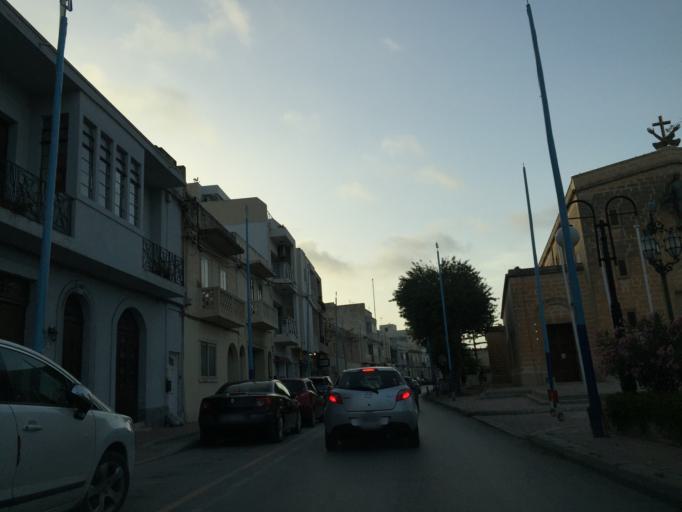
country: MT
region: Saint Paul's Bay
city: San Pawl il-Bahar
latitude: 35.9342
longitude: 14.4148
